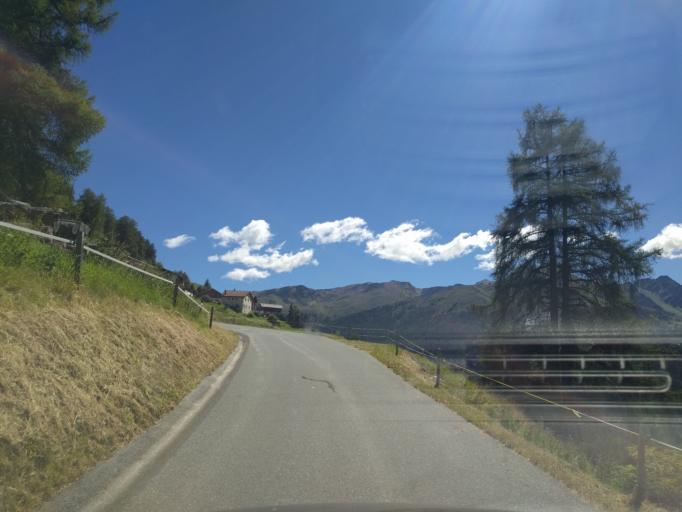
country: IT
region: Trentino-Alto Adige
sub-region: Bolzano
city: Tubre
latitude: 46.6101
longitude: 10.4035
